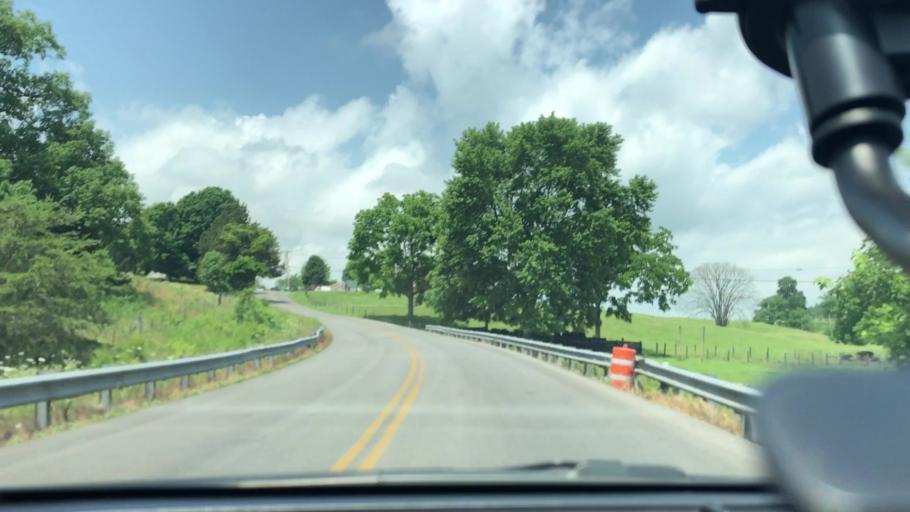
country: US
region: Kentucky
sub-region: Pulaski County
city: Somerset
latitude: 37.0592
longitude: -84.6639
